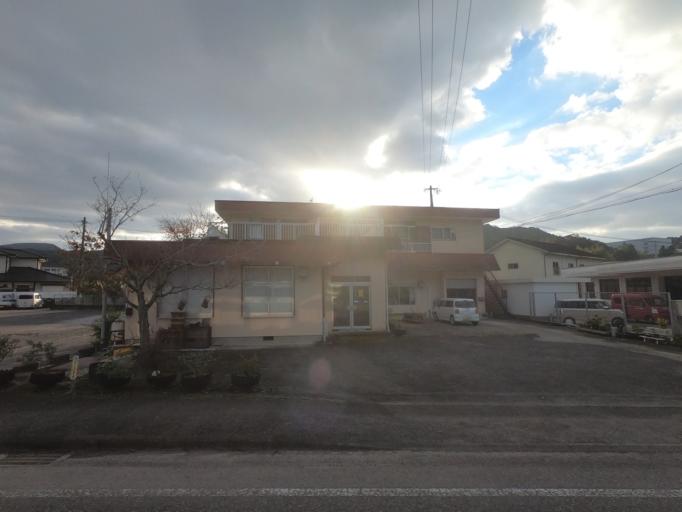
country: JP
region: Kumamoto
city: Minamata
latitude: 32.2711
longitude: 130.5023
